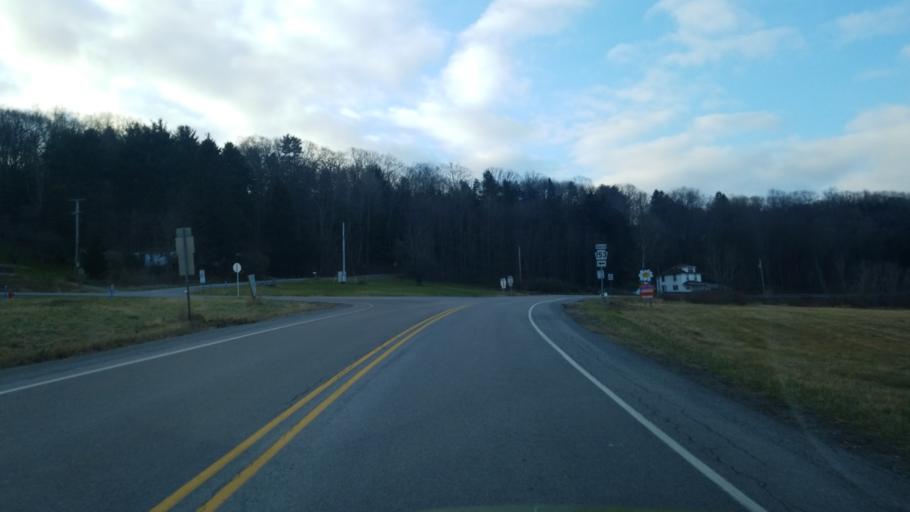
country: US
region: Pennsylvania
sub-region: Clearfield County
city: Clearfield
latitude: 41.0035
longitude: -78.4269
